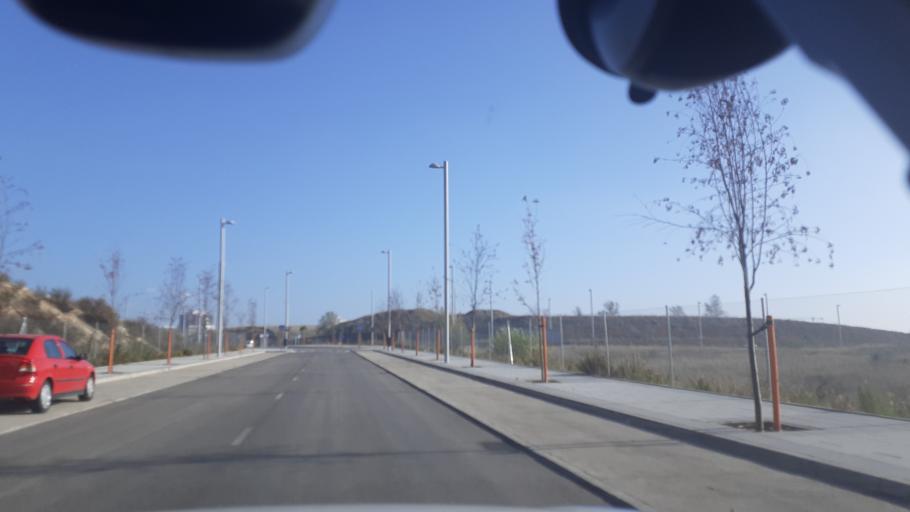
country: ES
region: Madrid
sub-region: Provincia de Madrid
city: Coslada
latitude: 40.4047
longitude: -3.5555
